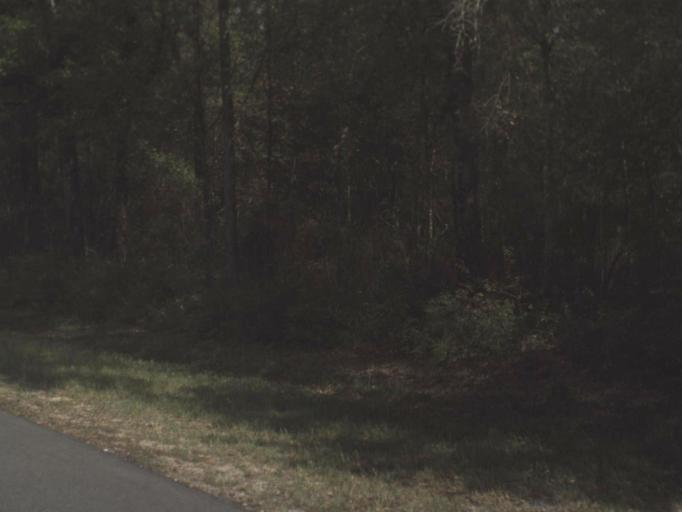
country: US
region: Florida
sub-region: Santa Rosa County
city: East Milton
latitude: 30.6418
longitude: -86.9418
